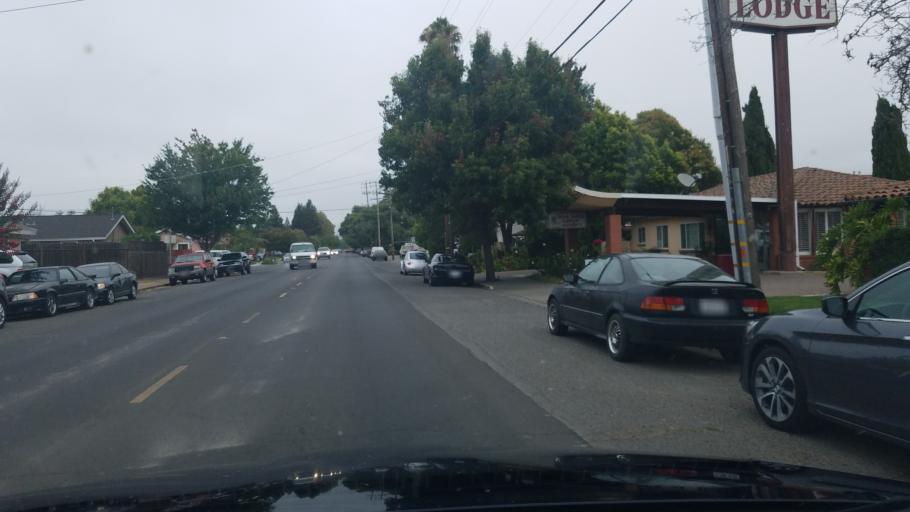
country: US
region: California
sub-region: Napa County
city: Napa
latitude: 38.2830
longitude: -122.2887
